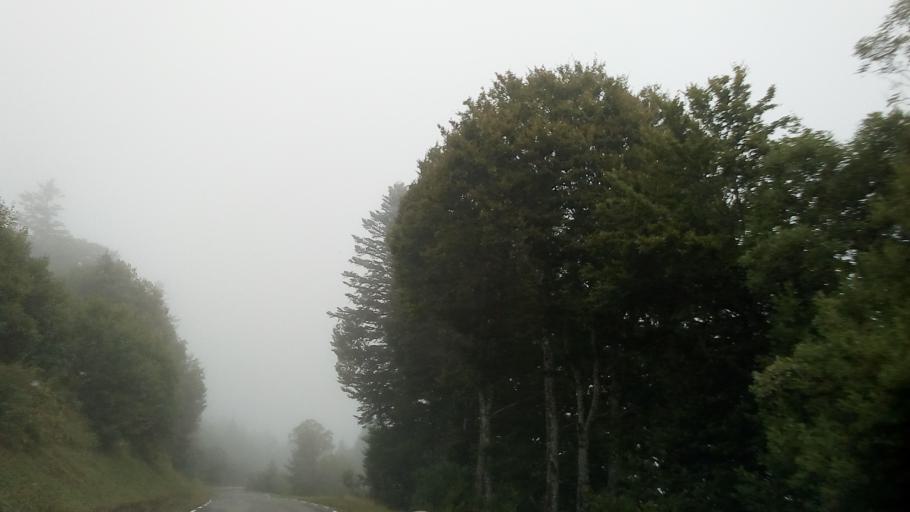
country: FR
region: Midi-Pyrenees
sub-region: Departement des Hautes-Pyrenees
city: Saint-Lary-Soulan
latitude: 42.7835
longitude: 0.1743
